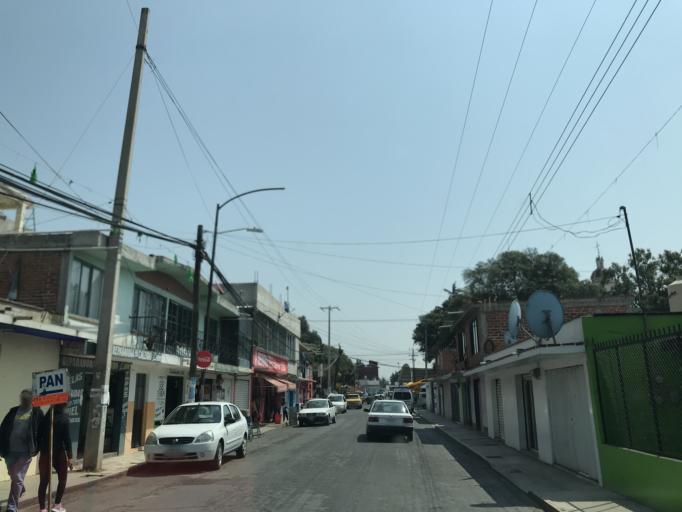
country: MX
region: Tlaxcala
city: Yauhquemehcan
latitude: 19.4055
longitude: -98.1832
